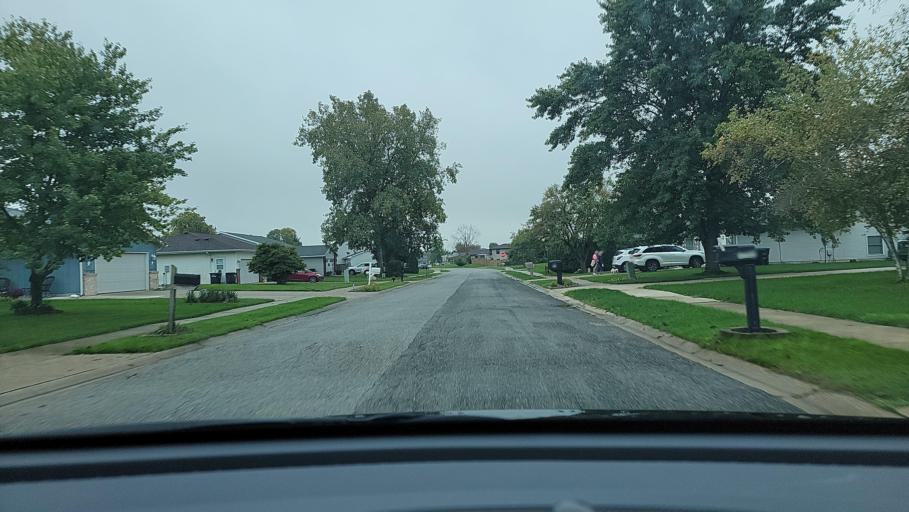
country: US
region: Indiana
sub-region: Porter County
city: Portage
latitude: 41.5447
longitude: -87.1930
